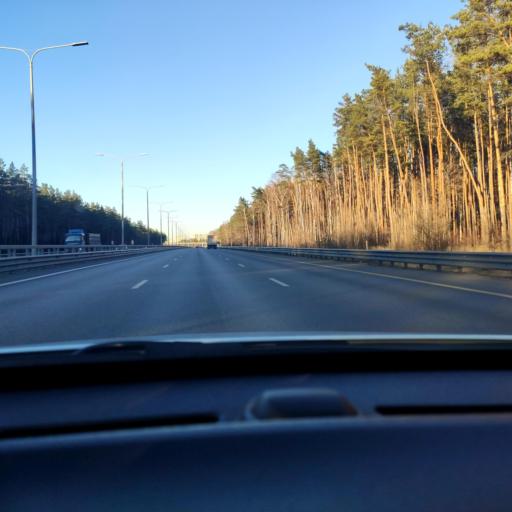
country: RU
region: Voronezj
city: Somovo
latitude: 51.7185
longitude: 39.3088
